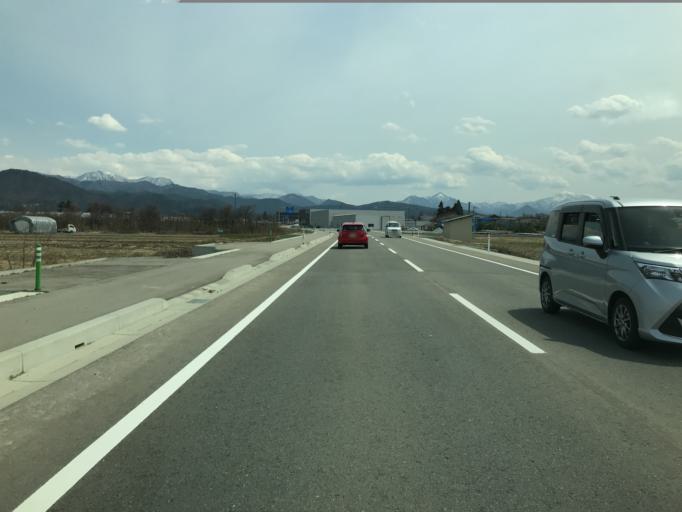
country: JP
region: Yamagata
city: Higashine
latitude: 38.4487
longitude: 140.3758
